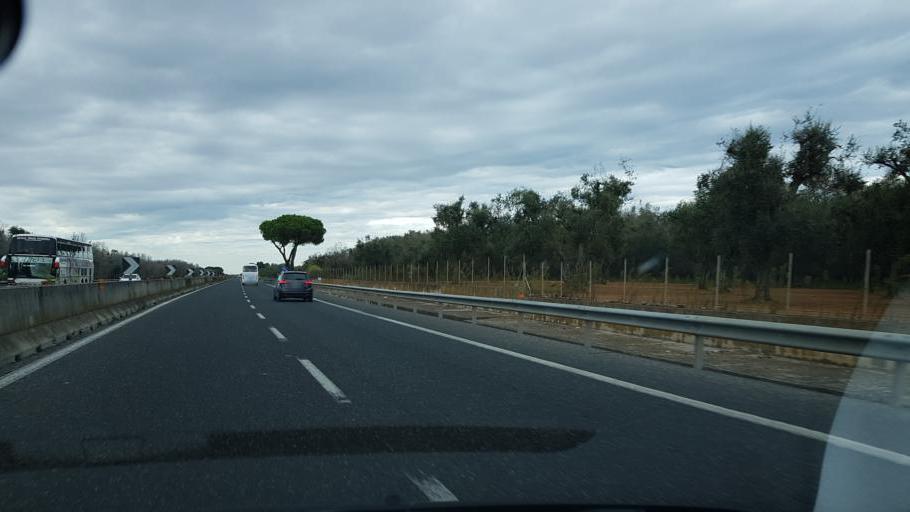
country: IT
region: Apulia
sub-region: Provincia di Brindisi
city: Torchiarolo
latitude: 40.4693
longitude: 18.0518
